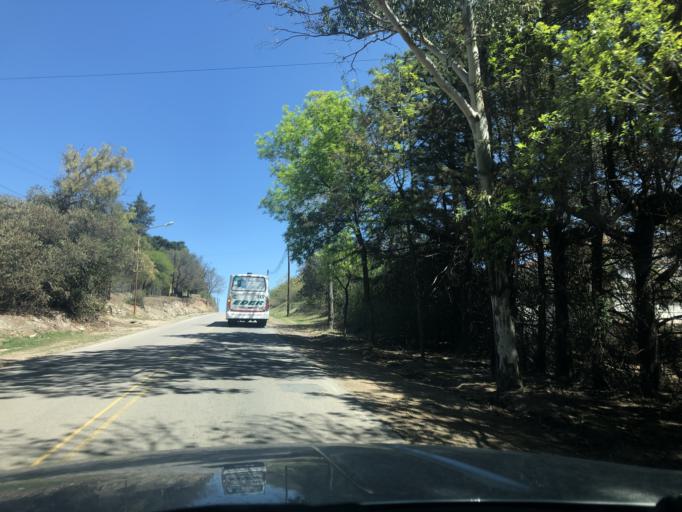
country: AR
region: Cordoba
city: La Granja
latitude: -31.0154
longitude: -64.2717
